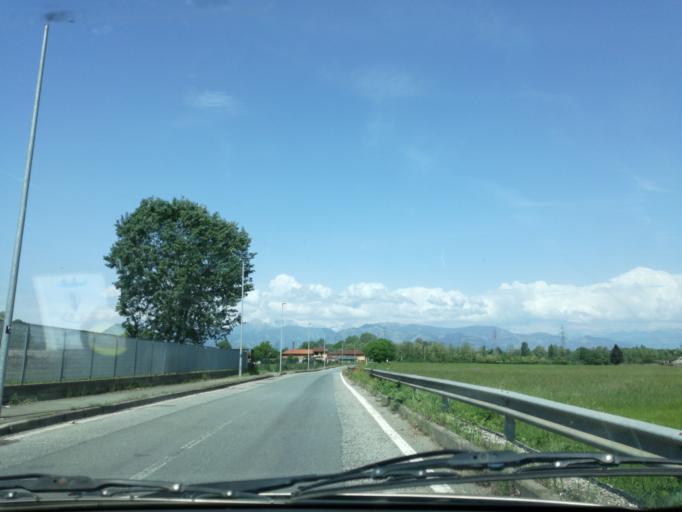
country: IT
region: Piedmont
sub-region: Provincia di Torino
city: Savonera
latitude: 45.0884
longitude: 7.6222
